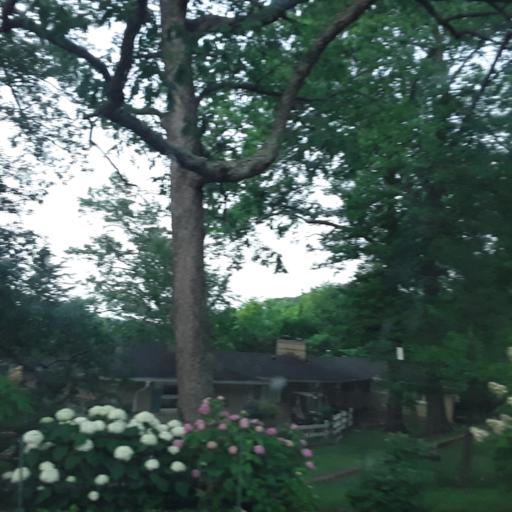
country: US
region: Tennessee
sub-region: Williamson County
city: Brentwood
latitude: 36.0567
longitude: -86.7809
